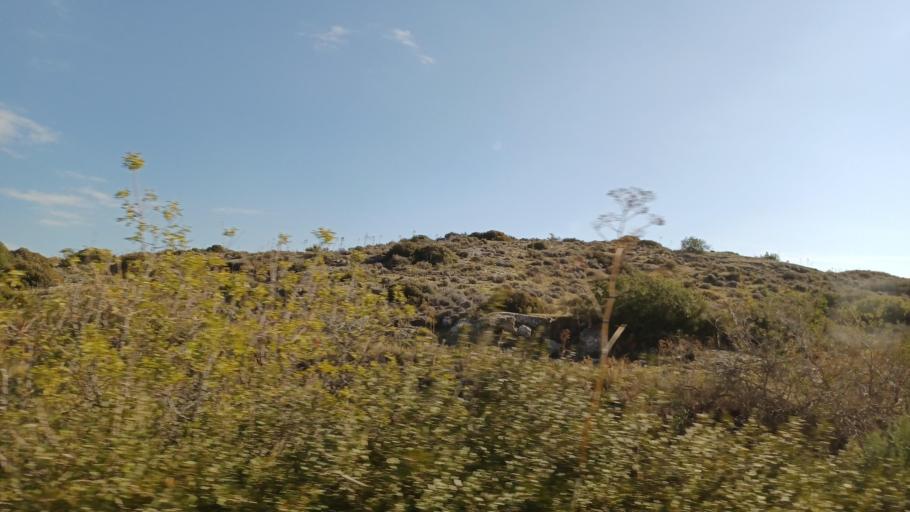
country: CY
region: Larnaka
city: Kofinou
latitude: 34.7680
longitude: 33.3269
